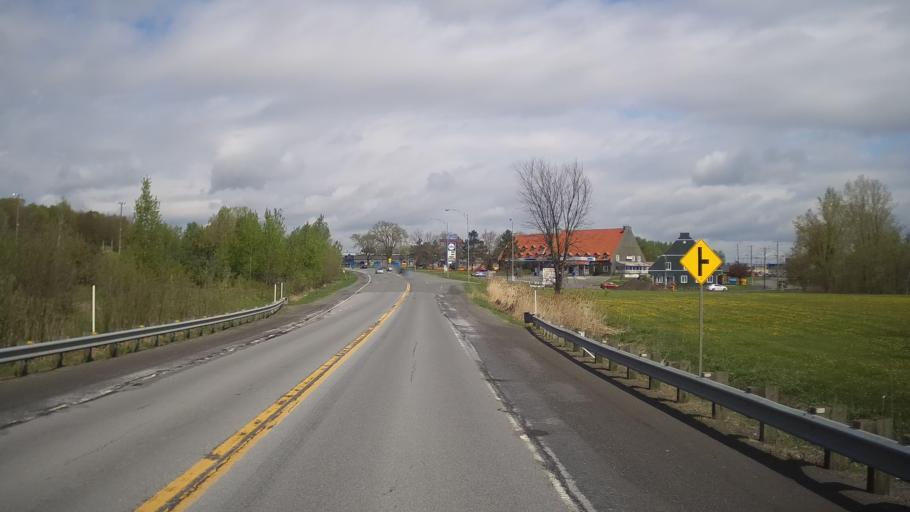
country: CA
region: Quebec
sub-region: Monteregie
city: Cowansville
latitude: 45.2068
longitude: -72.7673
